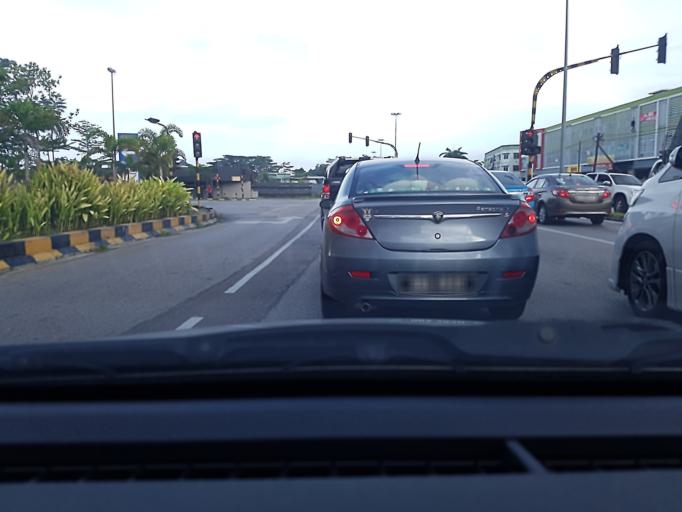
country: MY
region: Sarawak
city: Kuching
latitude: 1.5276
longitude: 110.3681
